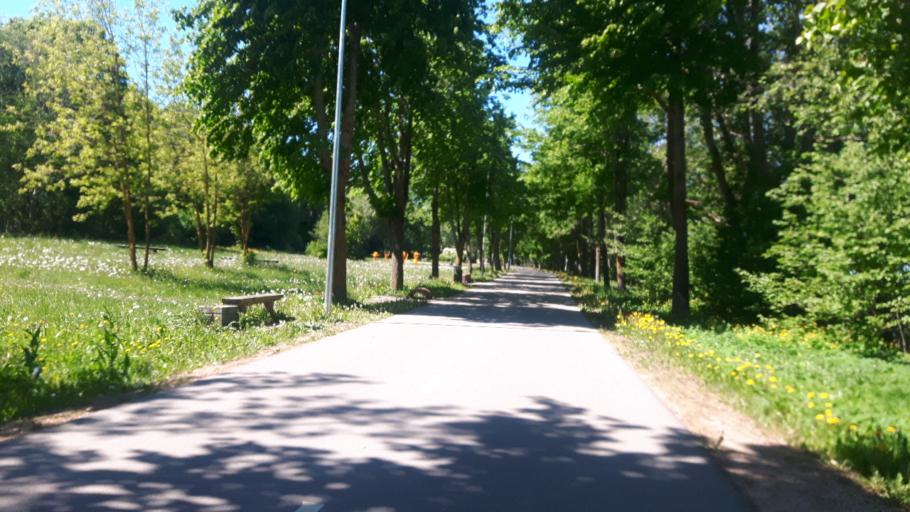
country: EE
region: Ida-Virumaa
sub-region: Sillamaee linn
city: Sillamae
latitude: 59.3964
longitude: 27.7844
